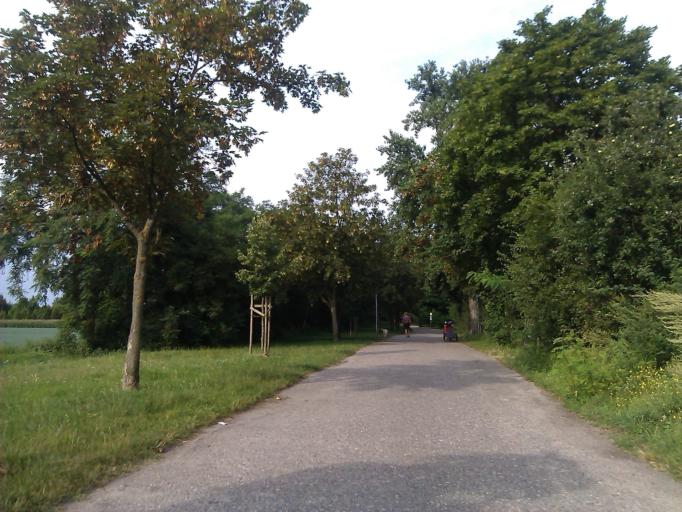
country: DE
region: Rheinland-Pfalz
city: Neuhofen
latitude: 49.4148
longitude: 8.4171
